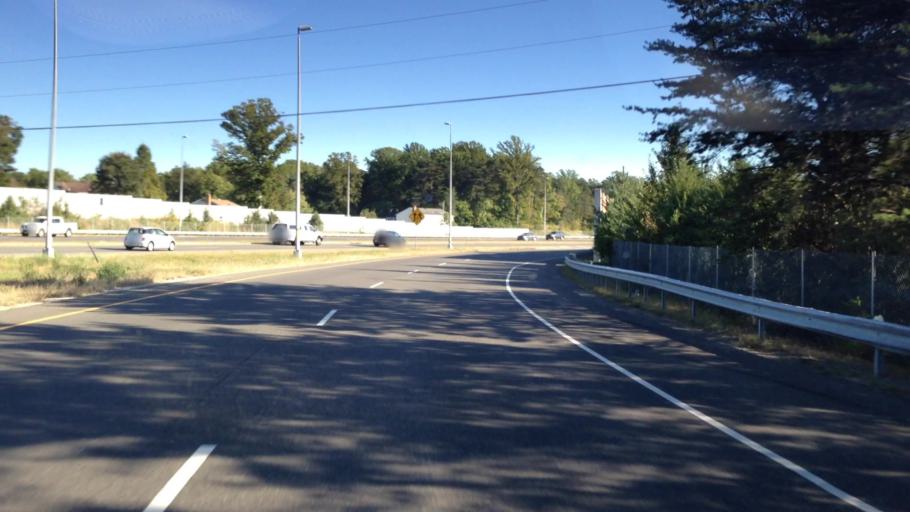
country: US
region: Virginia
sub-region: Fairfax County
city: West Springfield
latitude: 38.7579
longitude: -77.2165
